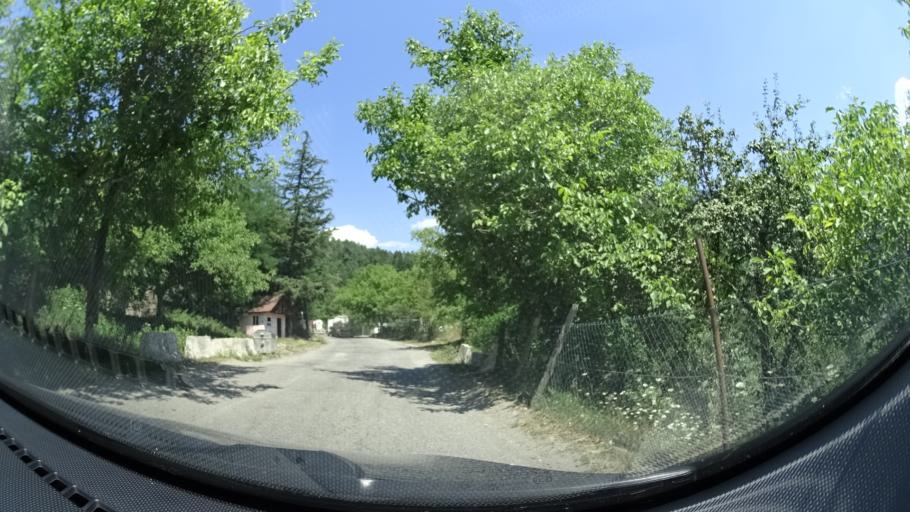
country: GE
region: Ajaria
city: Khulo
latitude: 41.6330
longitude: 42.2960
